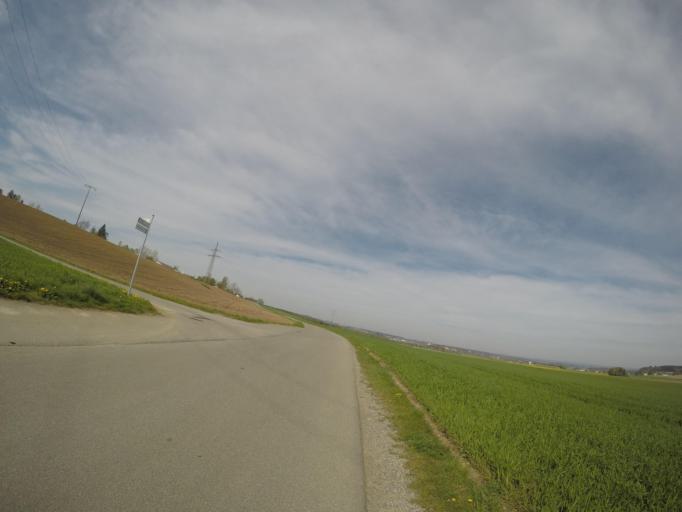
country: DE
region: Baden-Wuerttemberg
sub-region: Tuebingen Region
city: Boms
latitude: 48.0046
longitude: 9.5531
